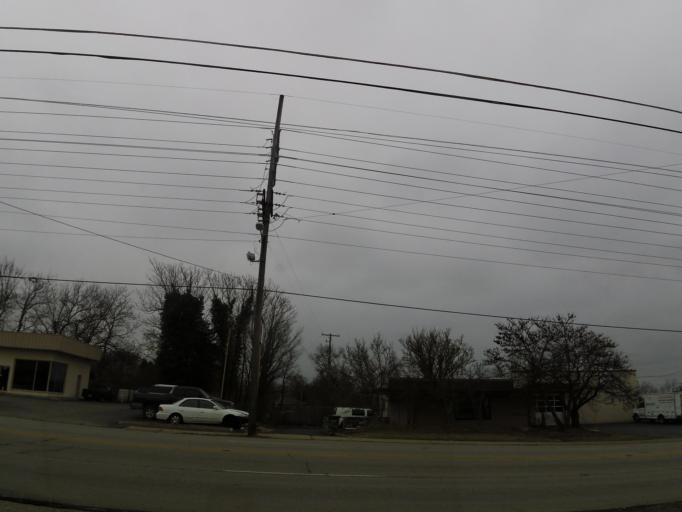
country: US
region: Kentucky
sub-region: Franklin County
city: Frankfort
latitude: 38.2030
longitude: -84.8484
